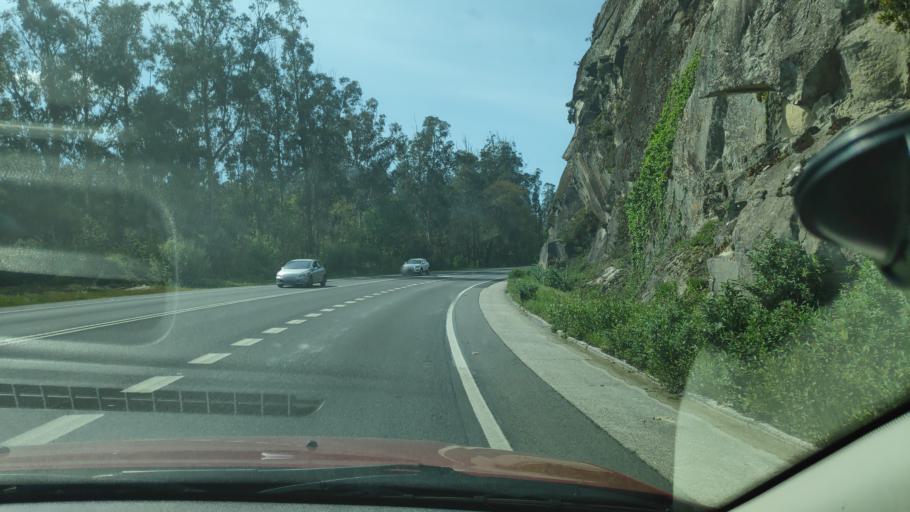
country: ES
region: Galicia
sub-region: Provincia da Coruna
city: Ames
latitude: 42.8760
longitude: -8.6717
